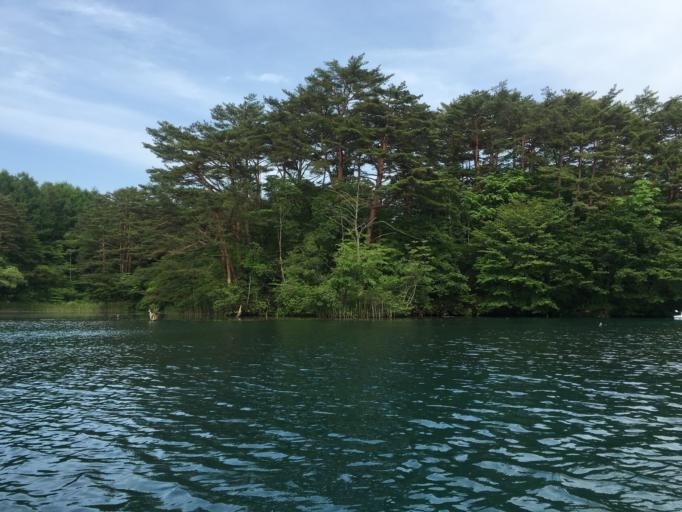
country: JP
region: Fukushima
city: Inawashiro
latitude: 37.6527
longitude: 140.0873
